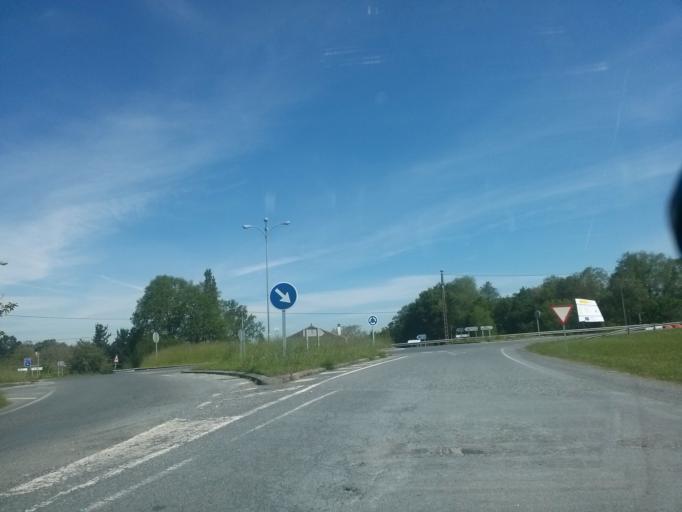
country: ES
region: Galicia
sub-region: Provincia de Lugo
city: Lugo
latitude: 42.9867
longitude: -7.5895
